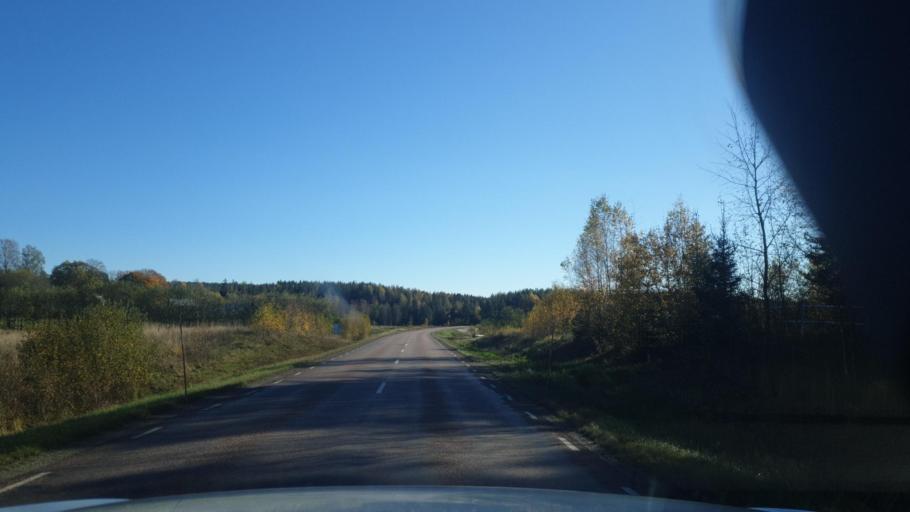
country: SE
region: Vaermland
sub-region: Grums Kommun
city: Slottsbron
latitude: 59.4125
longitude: 12.9946
